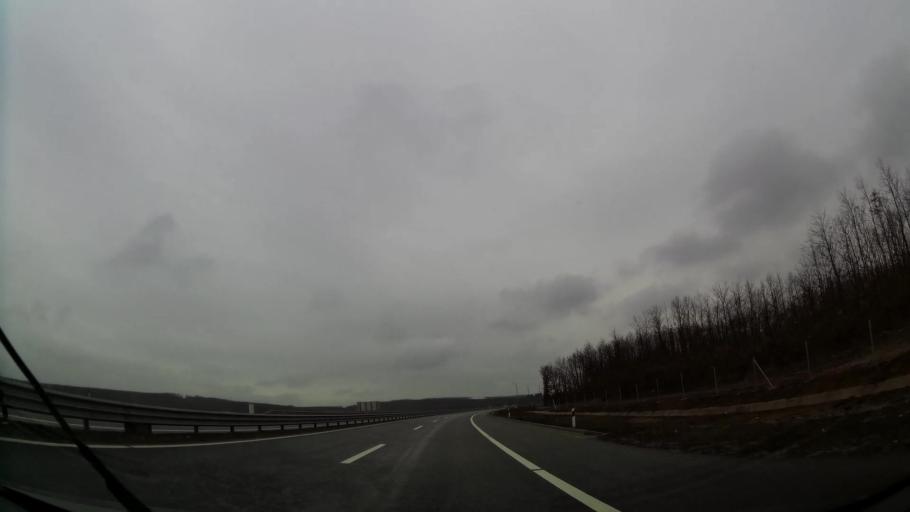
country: XK
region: Ferizaj
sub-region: Komuna e Ferizajt
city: Ferizaj
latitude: 42.3742
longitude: 21.2071
